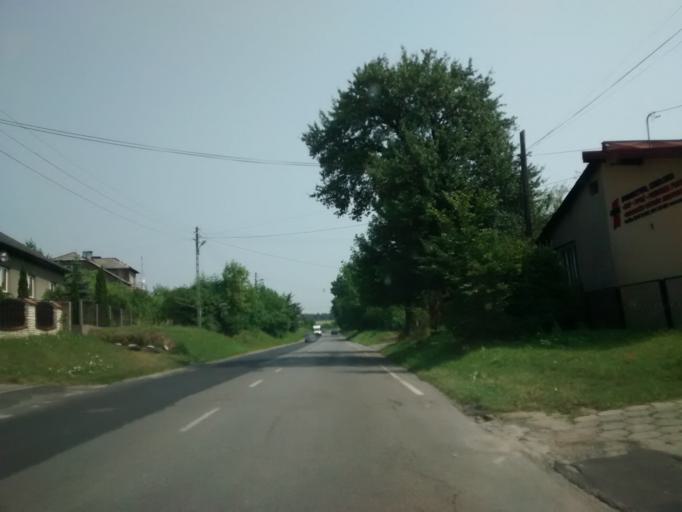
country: PL
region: Silesian Voivodeship
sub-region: Powiat zawiercianski
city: Ogrodzieniec
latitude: 50.4533
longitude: 19.5295
